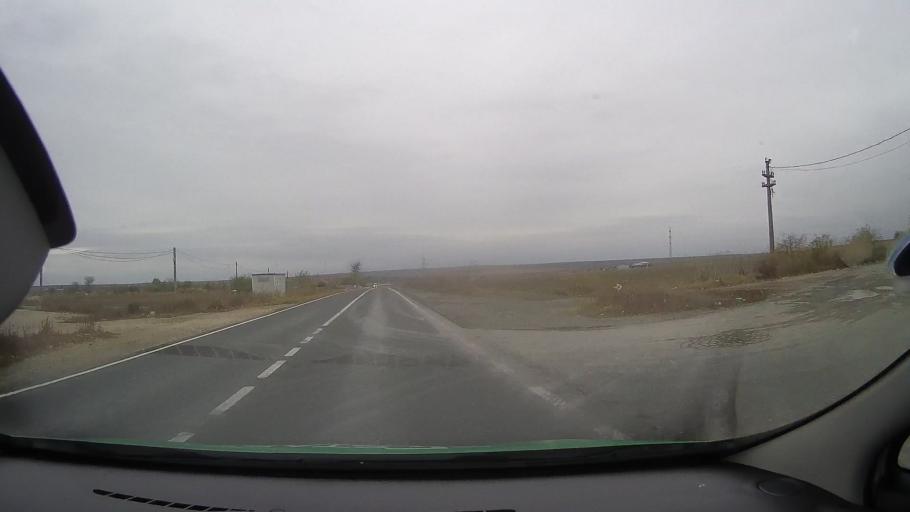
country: RO
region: Constanta
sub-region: Comuna Nicolae Balcescu
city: Dorobantu
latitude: 44.4213
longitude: 28.3119
